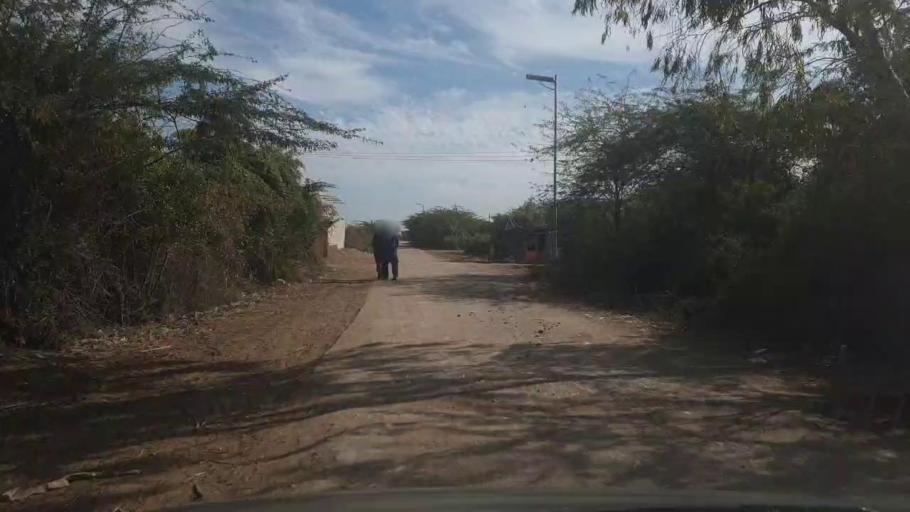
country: PK
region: Sindh
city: Pithoro
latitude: 25.3993
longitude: 69.2508
